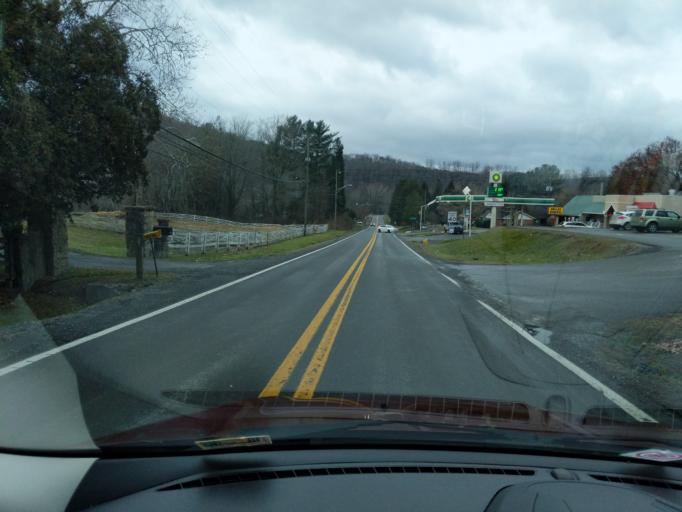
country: US
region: West Virginia
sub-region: Greenbrier County
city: Alderson
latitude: 37.7293
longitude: -80.6320
